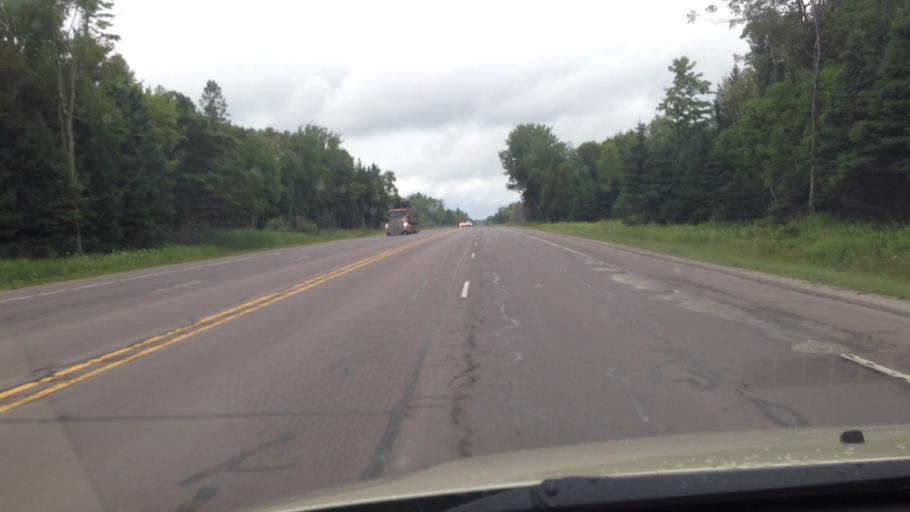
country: US
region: Michigan
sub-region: Schoolcraft County
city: Manistique
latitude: 46.0093
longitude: -85.9962
